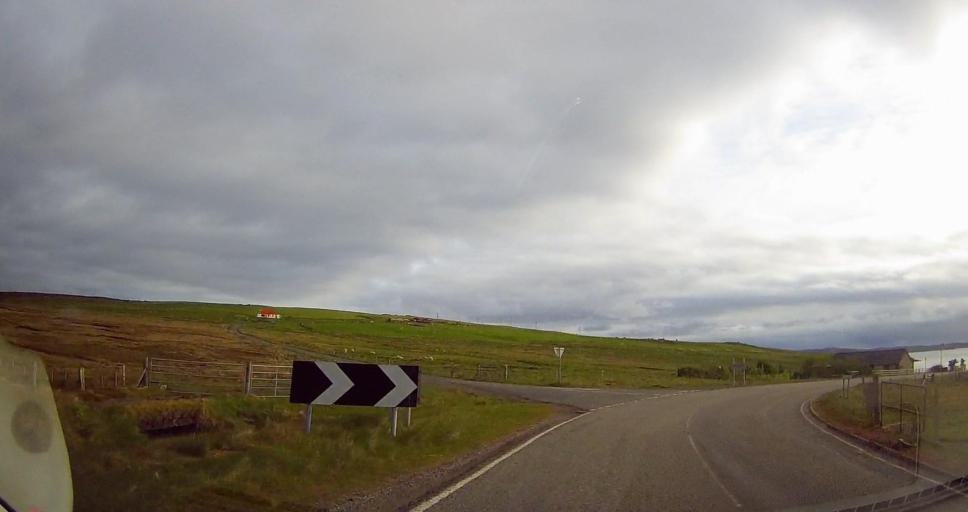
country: GB
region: Scotland
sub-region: Shetland Islands
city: Lerwick
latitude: 60.4662
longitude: -1.2122
